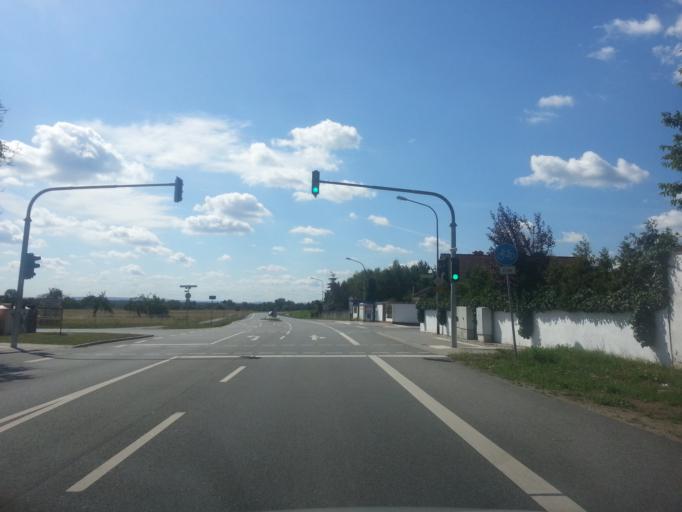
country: DE
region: Hesse
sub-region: Regierungsbezirk Darmstadt
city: Dietzenbach
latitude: 49.9964
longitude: 8.8202
